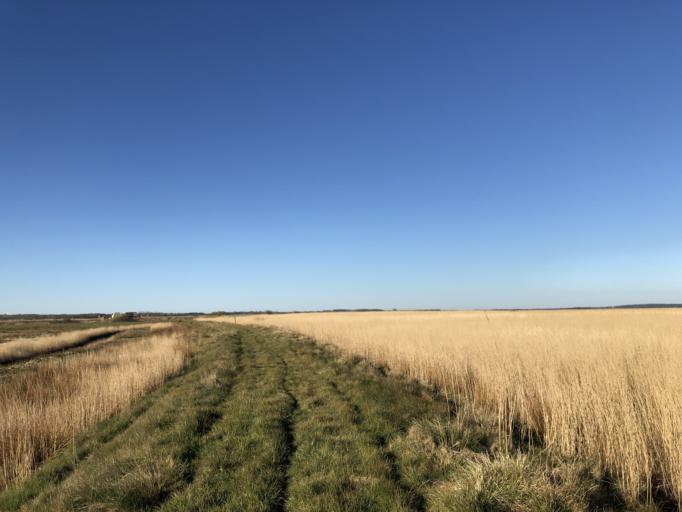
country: DK
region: Central Jutland
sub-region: Holstebro Kommune
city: Ulfborg
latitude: 56.2990
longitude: 8.2808
